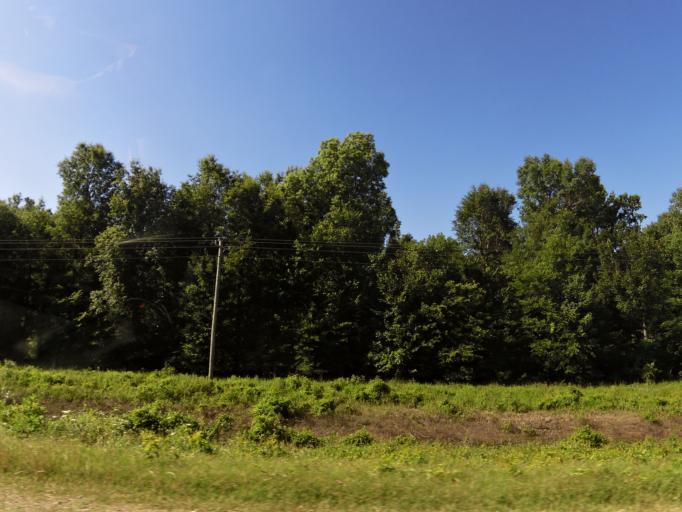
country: US
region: Arkansas
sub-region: Clay County
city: Corning
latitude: 36.4003
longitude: -90.5330
